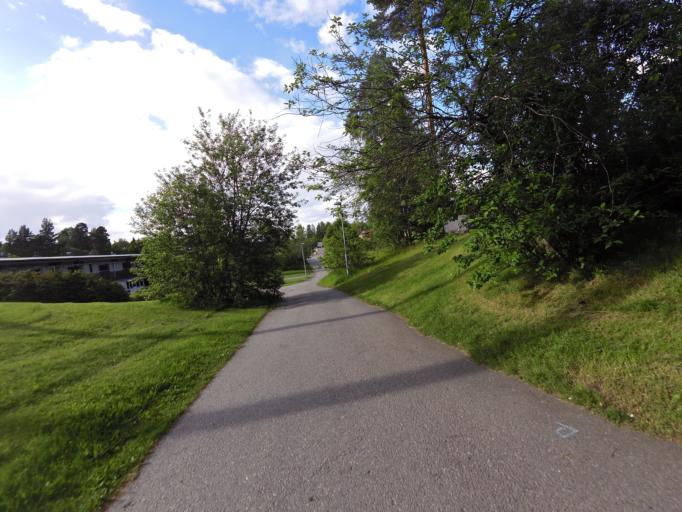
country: SE
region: Gaevleborg
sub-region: Gavle Kommun
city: Gavle
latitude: 60.6875
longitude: 17.1044
